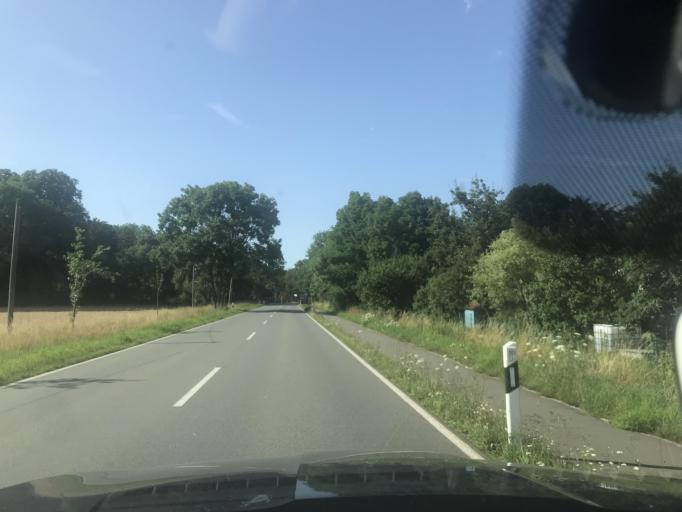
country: DE
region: Saxony-Anhalt
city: Wegeleben
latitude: 51.8798
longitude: 11.1759
